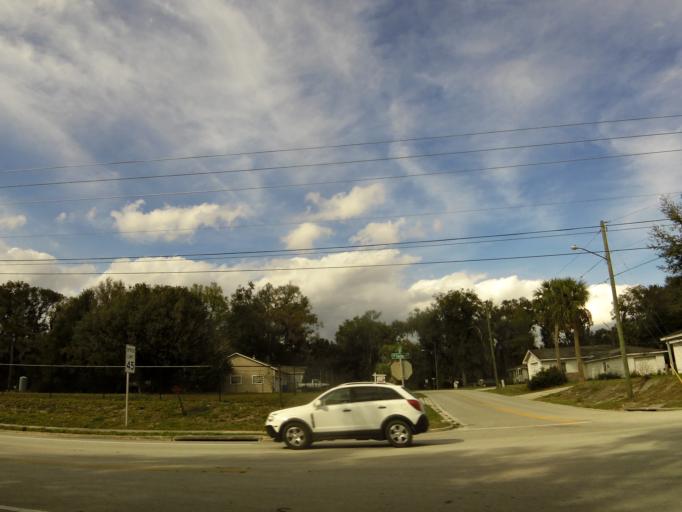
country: US
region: Florida
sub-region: Volusia County
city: De Land Southwest
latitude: 28.9989
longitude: -81.3071
